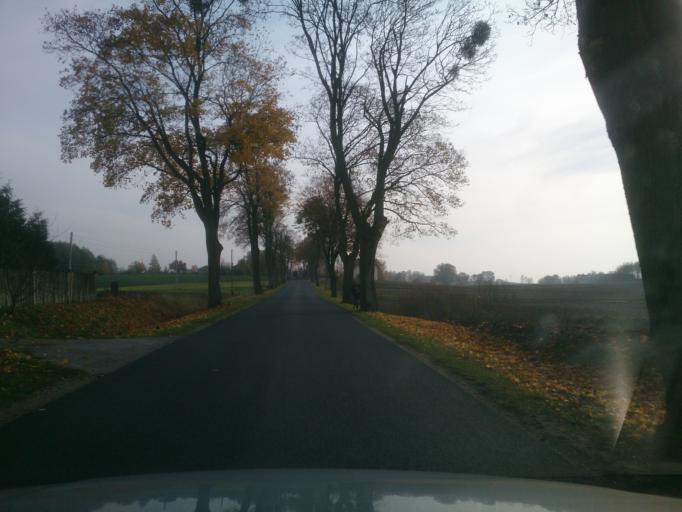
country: PL
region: Kujawsko-Pomorskie
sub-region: Powiat brodnicki
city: Brodnica
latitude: 53.3436
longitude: 19.3747
